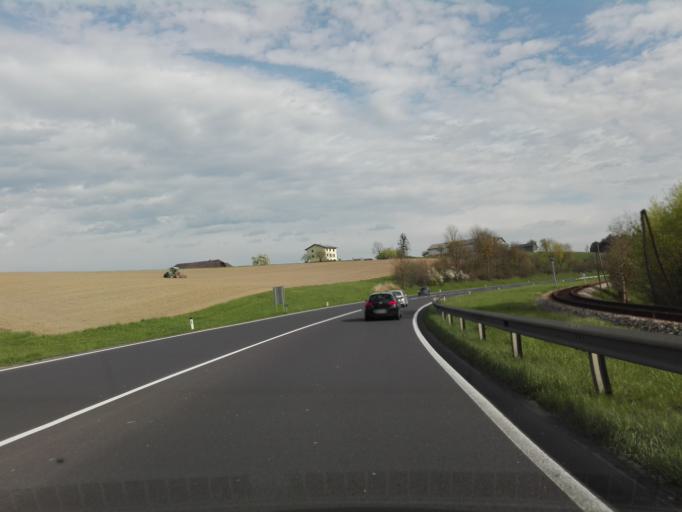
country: AT
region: Upper Austria
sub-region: Politischer Bezirk Urfahr-Umgebung
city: Herzogsdorf
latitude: 48.3926
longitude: 14.0874
